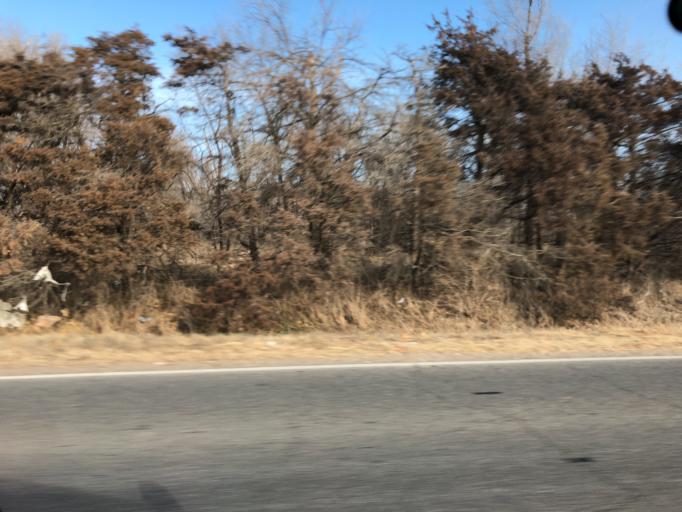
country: US
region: Kansas
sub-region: Reno County
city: Hutchinson
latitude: 38.0572
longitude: -97.9709
